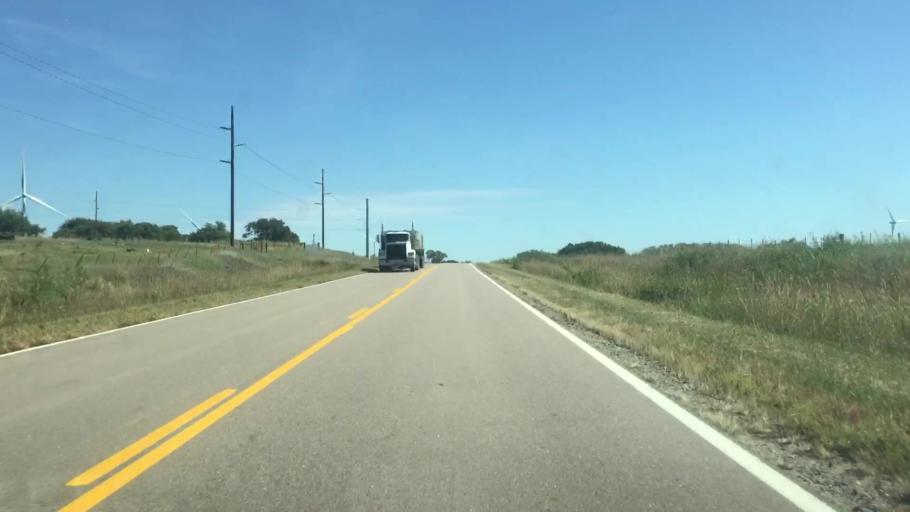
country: US
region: Nebraska
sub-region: Jefferson County
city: Fairbury
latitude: 40.0451
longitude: -96.9573
